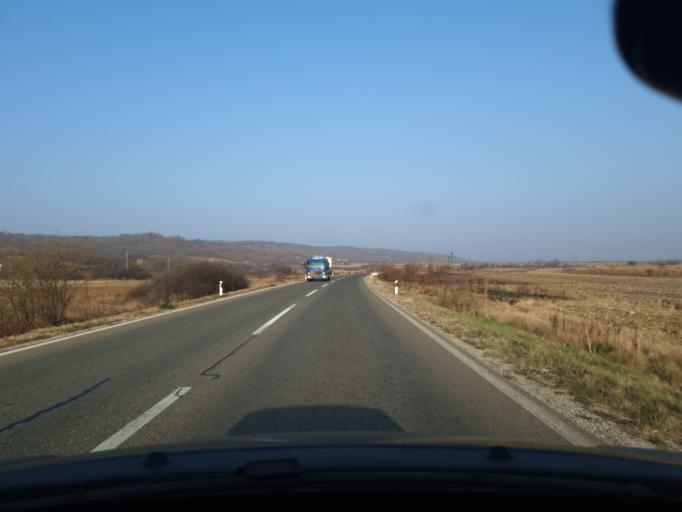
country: RS
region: Central Serbia
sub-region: Jablanicki Okrug
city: Leskovac
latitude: 42.9416
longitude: 21.9961
